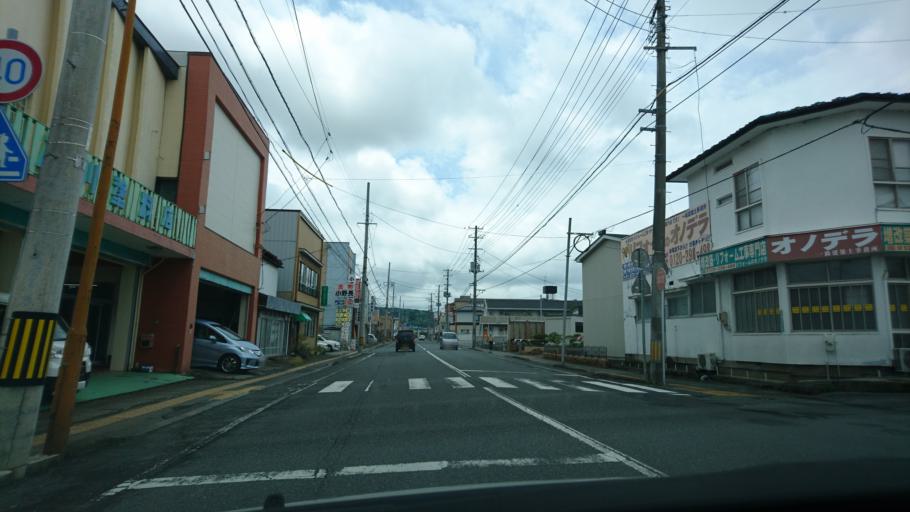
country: JP
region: Iwate
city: Ichinoseki
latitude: 38.9319
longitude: 141.1288
